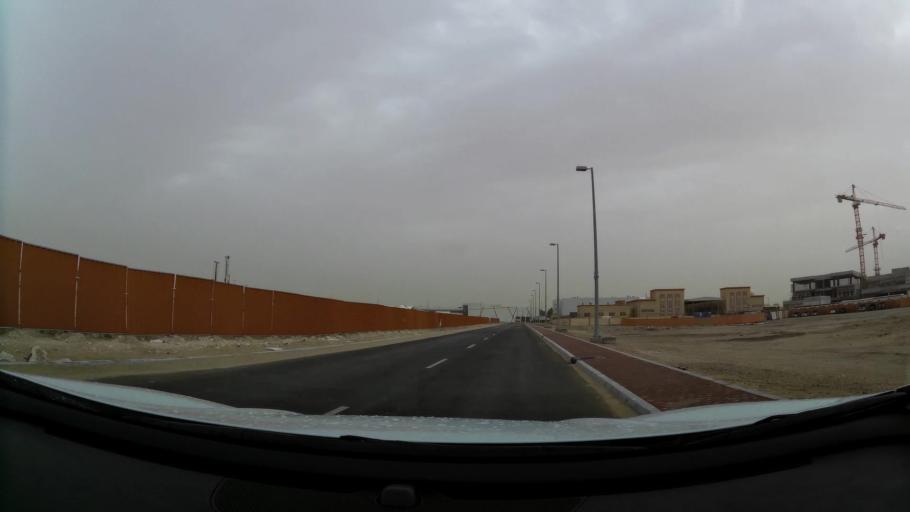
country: AE
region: Abu Dhabi
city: Abu Dhabi
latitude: 24.4311
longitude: 54.5811
